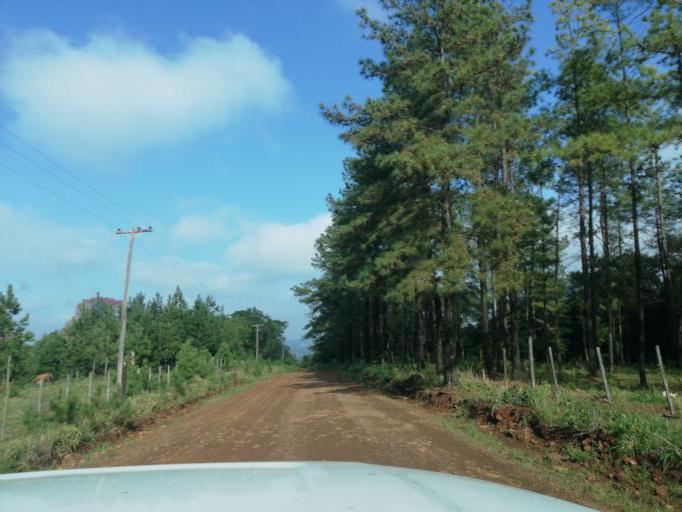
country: AR
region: Misiones
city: Cerro Azul
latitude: -27.5781
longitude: -55.5101
